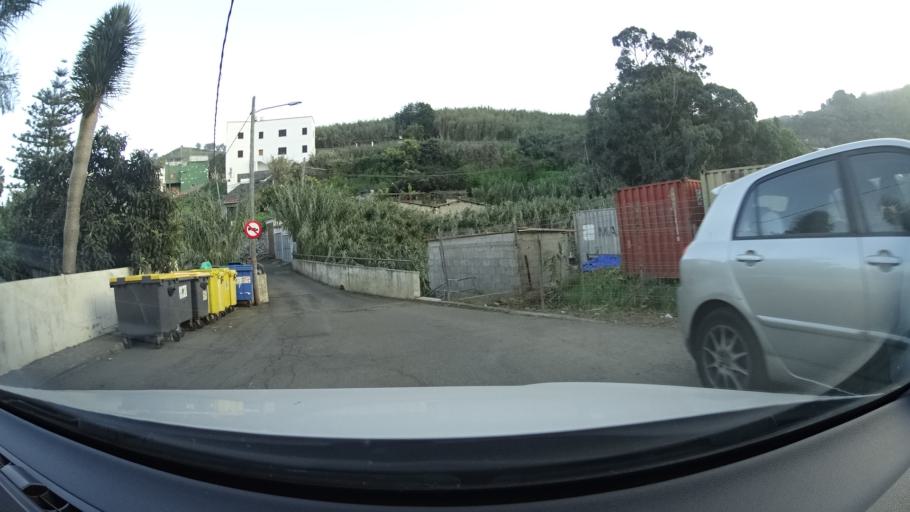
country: ES
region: Canary Islands
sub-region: Provincia de Las Palmas
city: Teror
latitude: 28.0583
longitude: -15.5448
